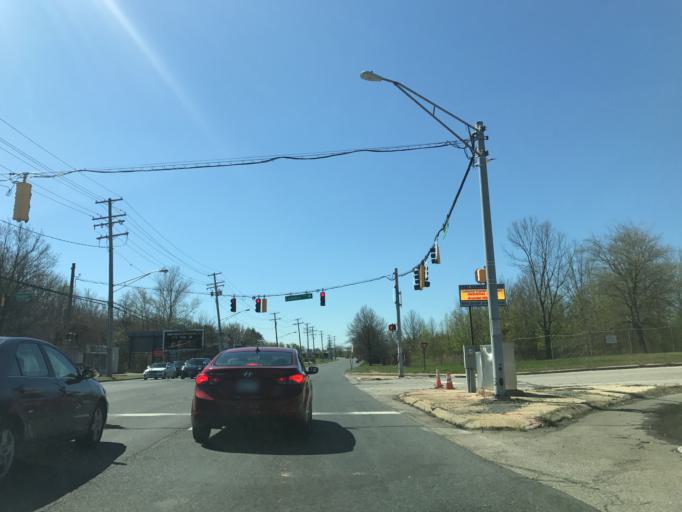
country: US
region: Maryland
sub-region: Anne Arundel County
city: Fort Meade
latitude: 39.1005
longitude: -76.7208
